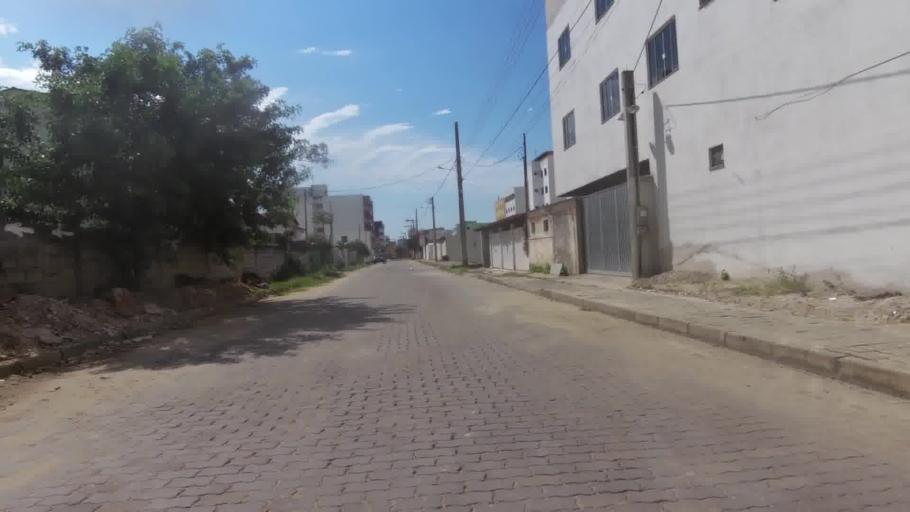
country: BR
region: Espirito Santo
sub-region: Piuma
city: Piuma
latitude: -20.8444
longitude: -40.7401
